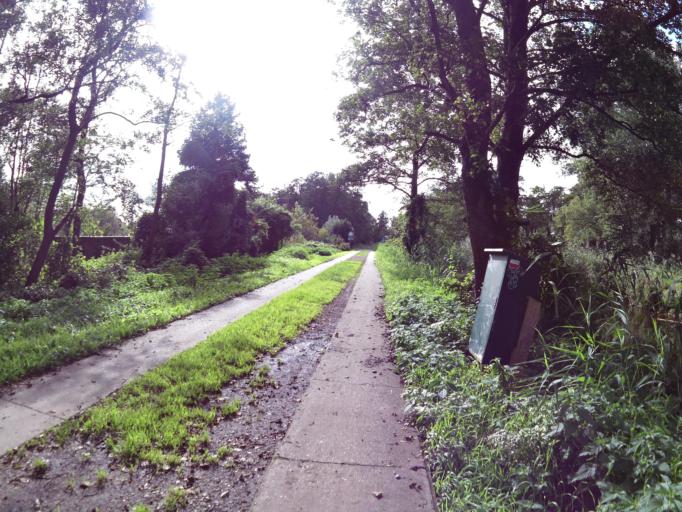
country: NL
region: North Holland
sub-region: Gemeente Wijdemeren
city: Oud-Loosdrecht
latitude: 52.1759
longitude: 5.0943
